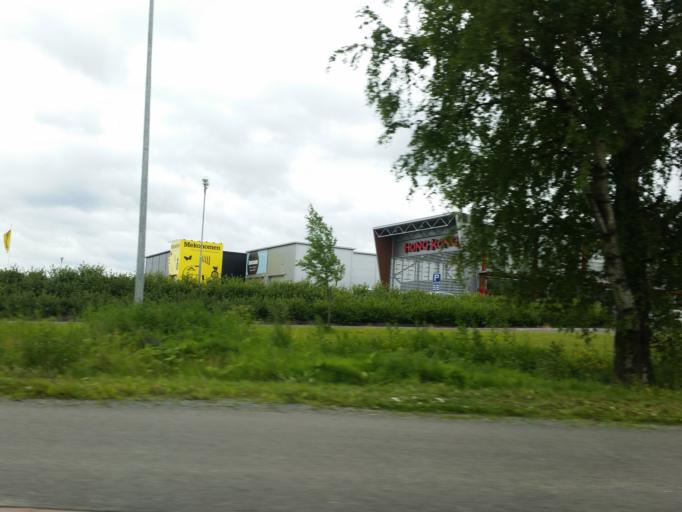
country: FI
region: Northern Savo
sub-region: Kuopio
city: Kuopio
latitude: 62.8742
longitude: 27.6227
